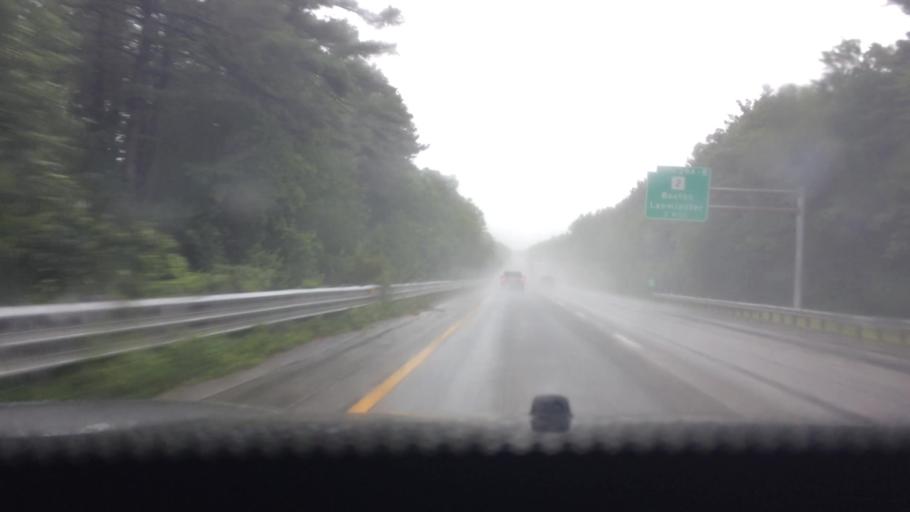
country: US
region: Massachusetts
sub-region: Worcester County
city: Harvard
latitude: 42.5065
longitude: -71.5246
